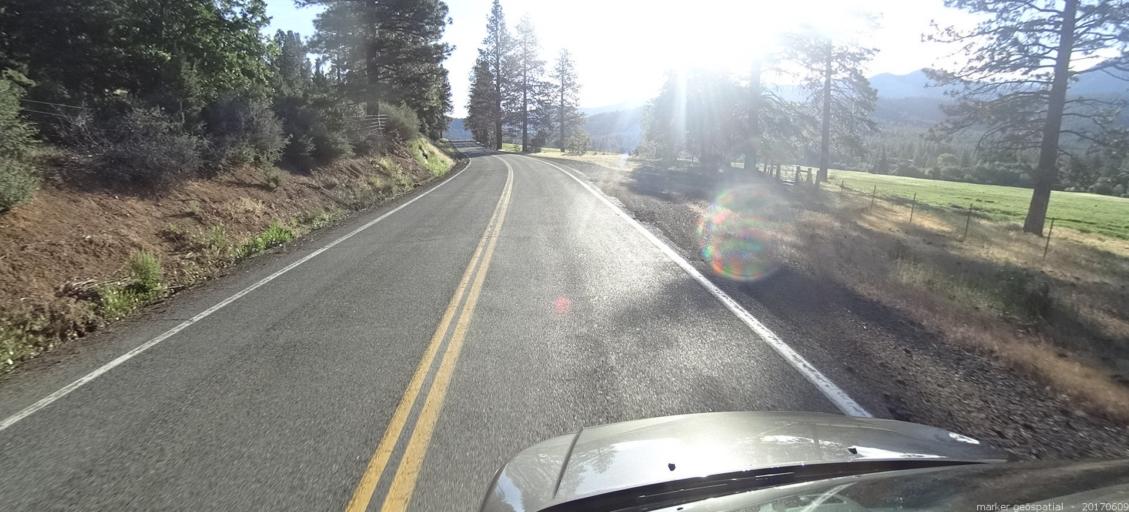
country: US
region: California
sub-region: Siskiyou County
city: Weed
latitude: 41.3851
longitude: -122.6830
